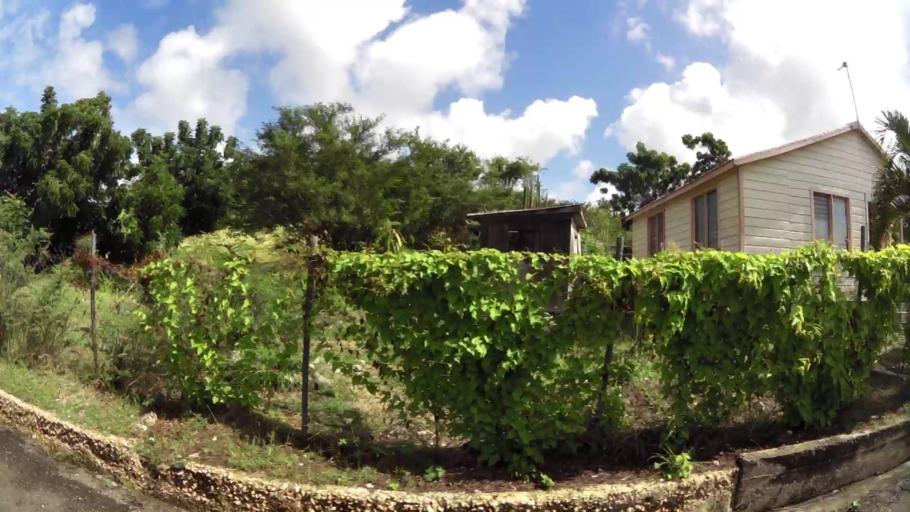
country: AG
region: Saint Mary
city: Bolands
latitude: 17.0676
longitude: -61.8740
